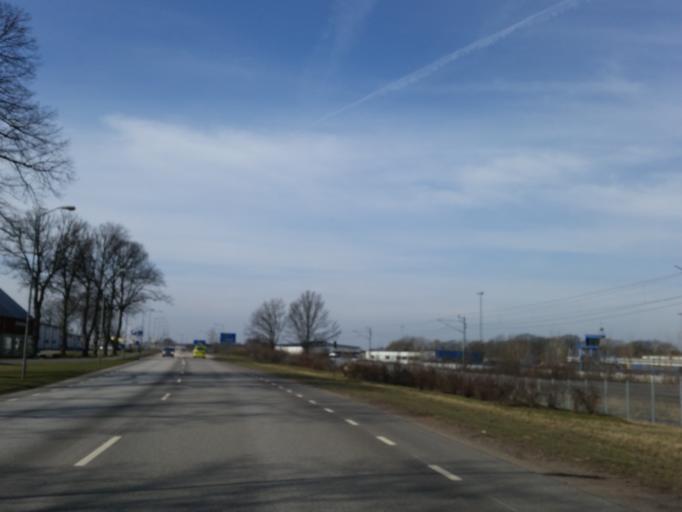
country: SE
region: Kalmar
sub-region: Kalmar Kommun
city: Kalmar
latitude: 56.6712
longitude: 16.3149
